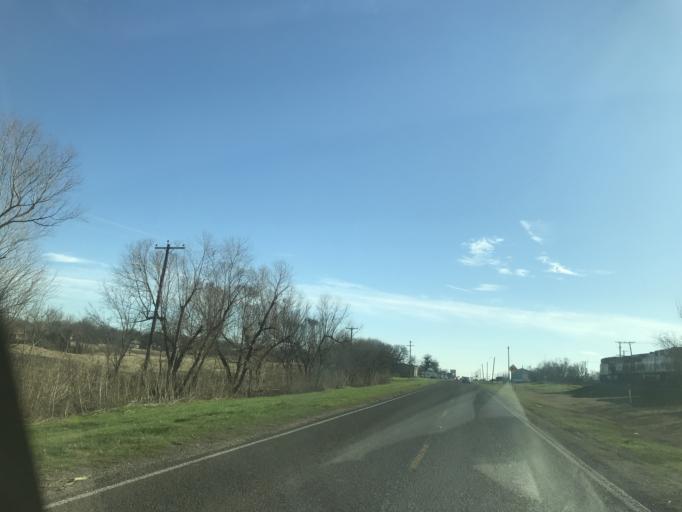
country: US
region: Texas
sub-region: Ellis County
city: Ferris
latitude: 32.5410
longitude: -96.6653
